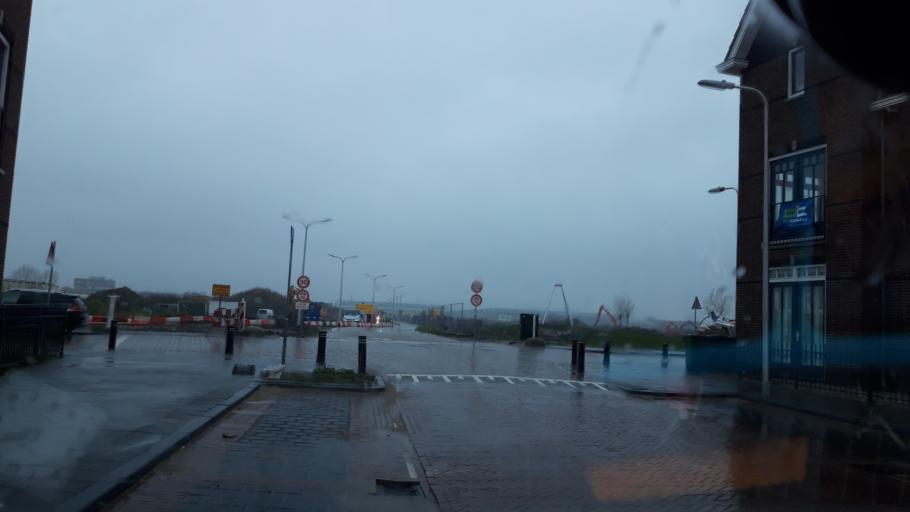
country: NL
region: South Holland
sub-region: Gemeente Westland
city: Poeldijk
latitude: 52.0277
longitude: 4.2229
